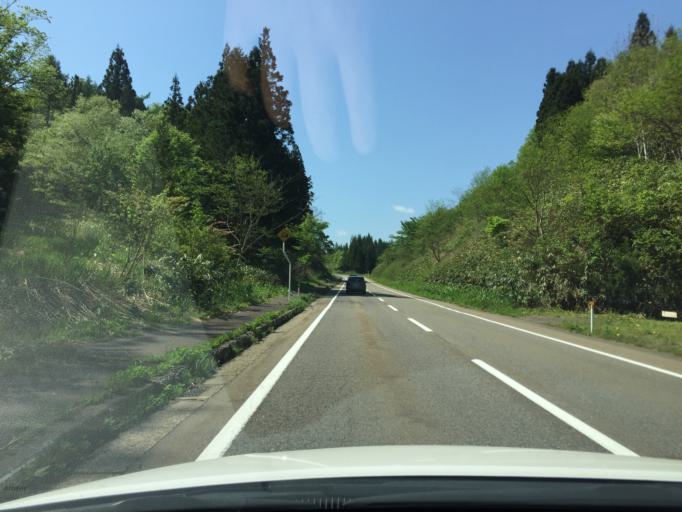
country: JP
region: Niigata
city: Kamo
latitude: 37.5962
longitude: 139.0942
